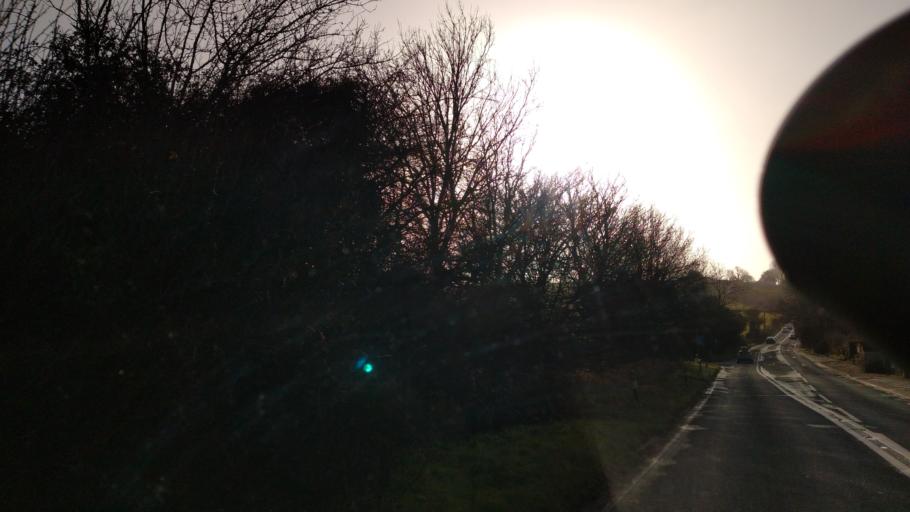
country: GB
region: England
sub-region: Somerset
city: Evercreech
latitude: 51.1455
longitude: -2.5472
